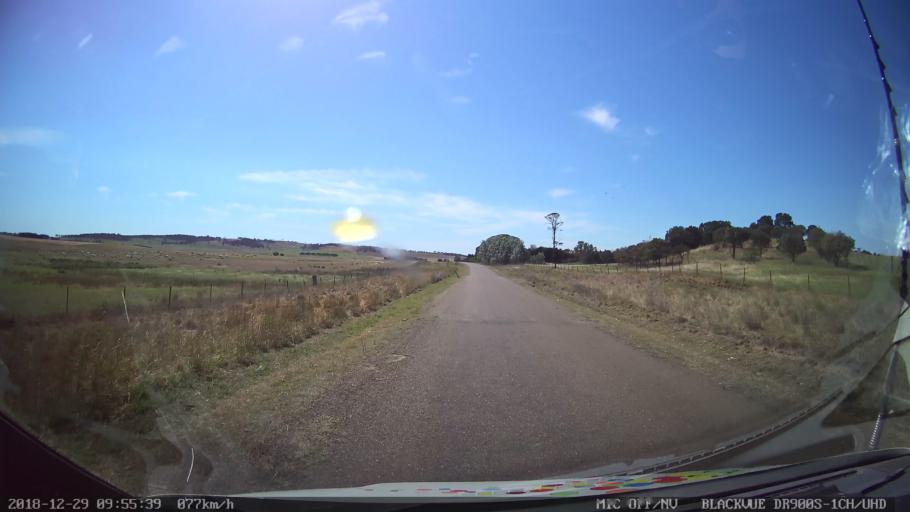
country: AU
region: New South Wales
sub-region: Goulburn Mulwaree
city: Goulburn
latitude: -34.7728
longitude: 149.4698
